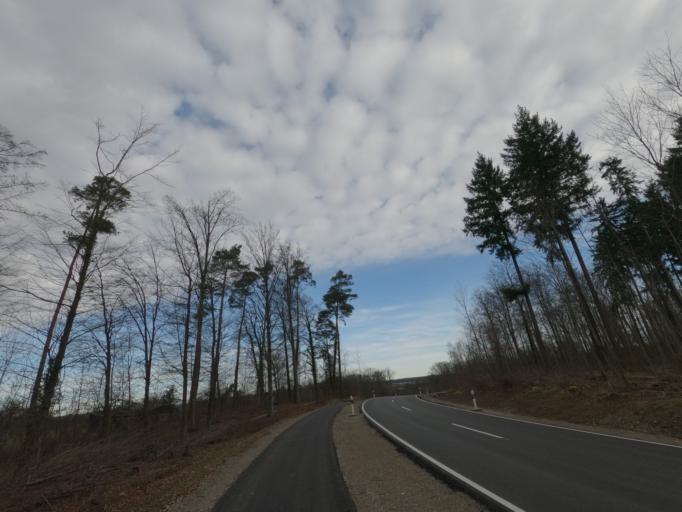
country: DE
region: Baden-Wuerttemberg
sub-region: Regierungsbezirk Stuttgart
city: Schlierbach
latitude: 48.6626
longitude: 9.5275
